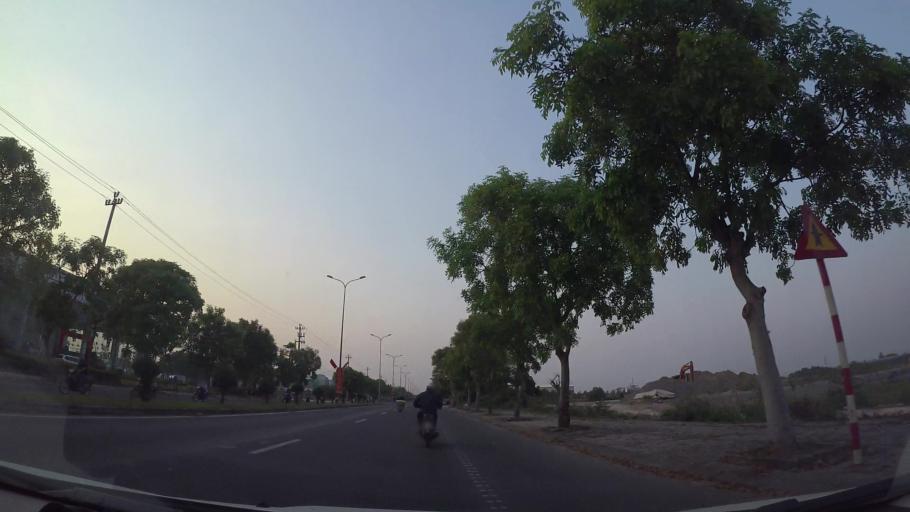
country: VN
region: Da Nang
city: Cam Le
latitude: 15.9635
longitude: 108.2126
